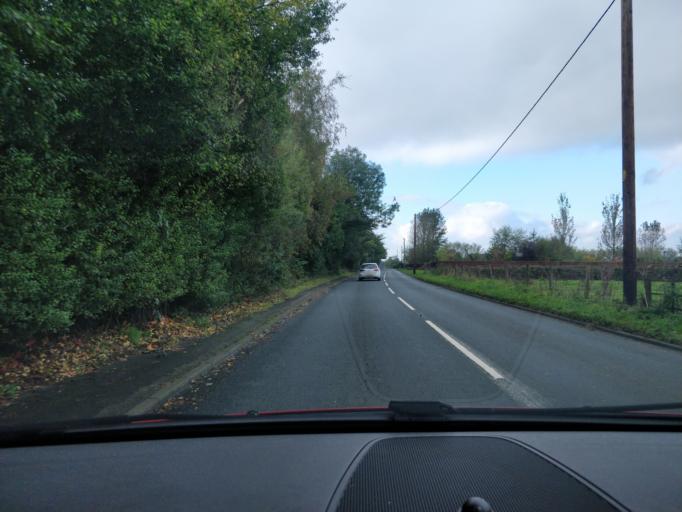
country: GB
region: England
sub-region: Lancashire
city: Ormskirk
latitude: 53.5818
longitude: -2.9017
